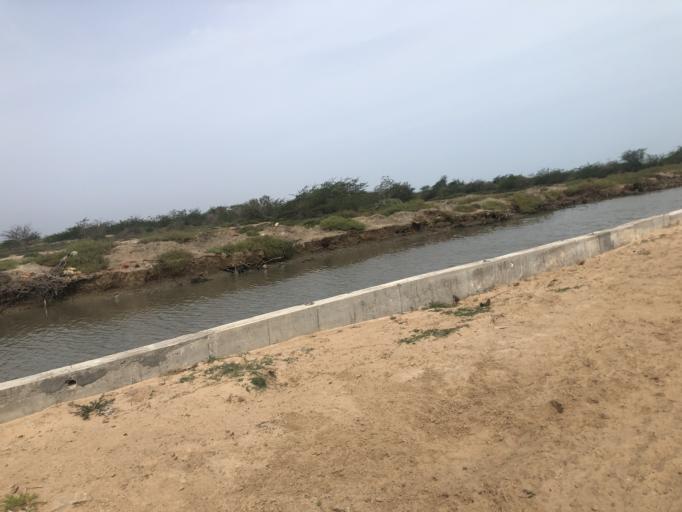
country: IN
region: Tamil Nadu
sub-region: Thanjavur
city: Adirampattinam
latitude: 10.3178
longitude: 79.3814
